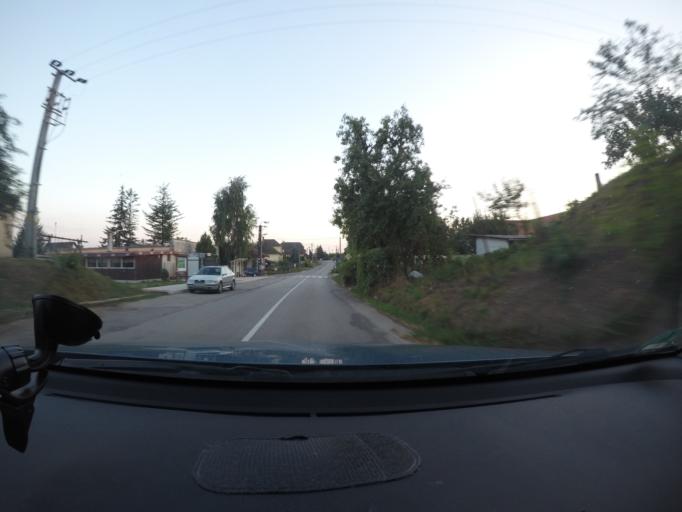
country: SK
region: Trenciansky
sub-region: Okres Nove Mesto nad Vahom
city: Nove Mesto nad Vahom
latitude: 48.8323
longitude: 17.9043
